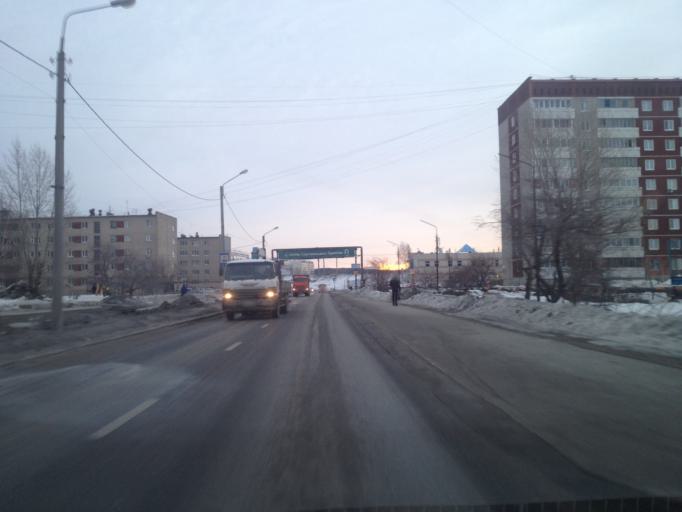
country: RU
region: Sverdlovsk
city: Sovkhoznyy
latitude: 56.7560
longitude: 60.6060
